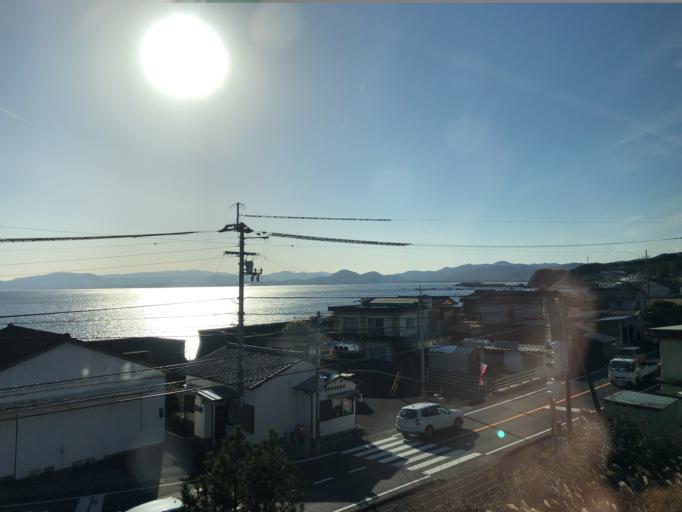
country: JP
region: Kochi
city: Nakamura
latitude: 33.0380
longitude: 133.0730
